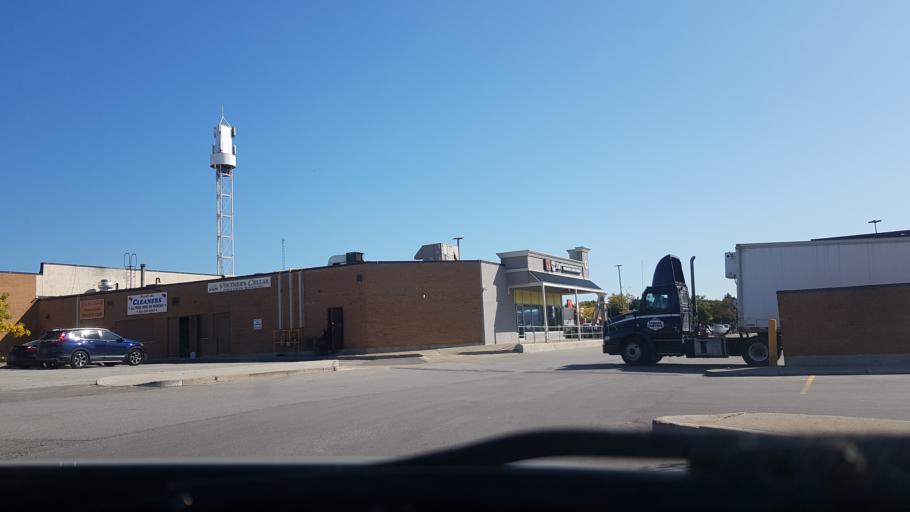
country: CA
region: Ontario
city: Brampton
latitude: 43.7274
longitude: -79.7982
